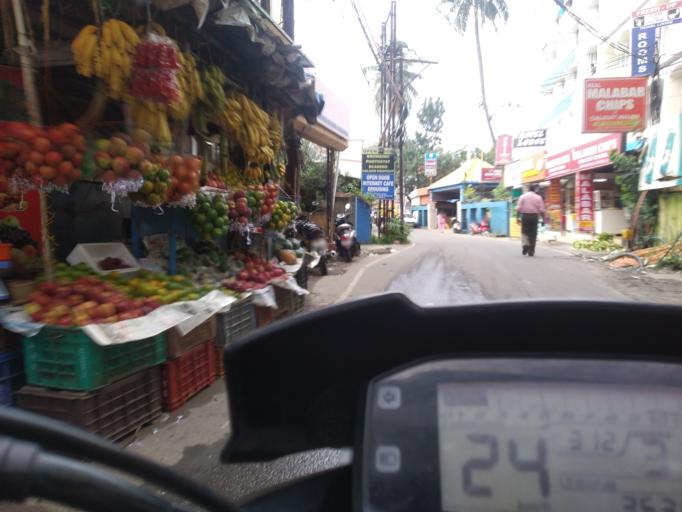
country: IN
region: Kerala
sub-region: Ernakulam
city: Cochin
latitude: 9.9684
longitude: 76.2893
